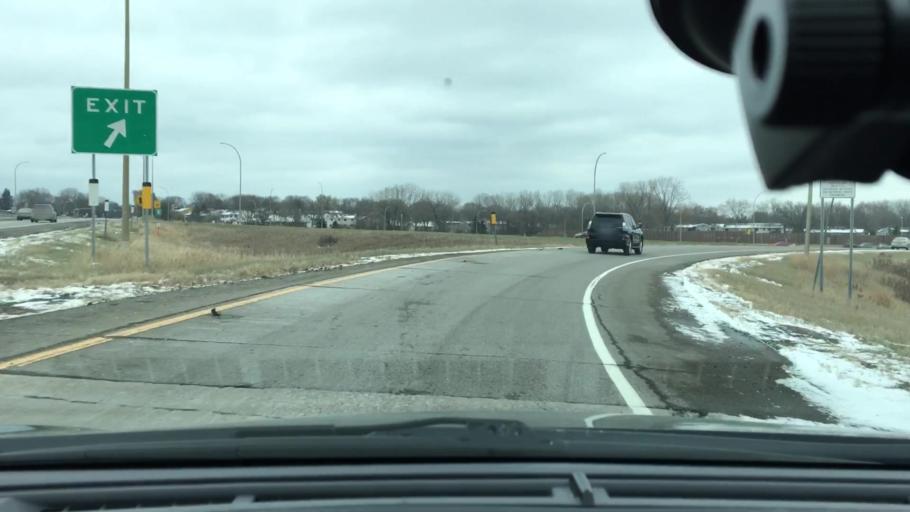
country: US
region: Minnesota
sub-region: Hennepin County
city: New Hope
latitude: 45.0331
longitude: -93.4036
